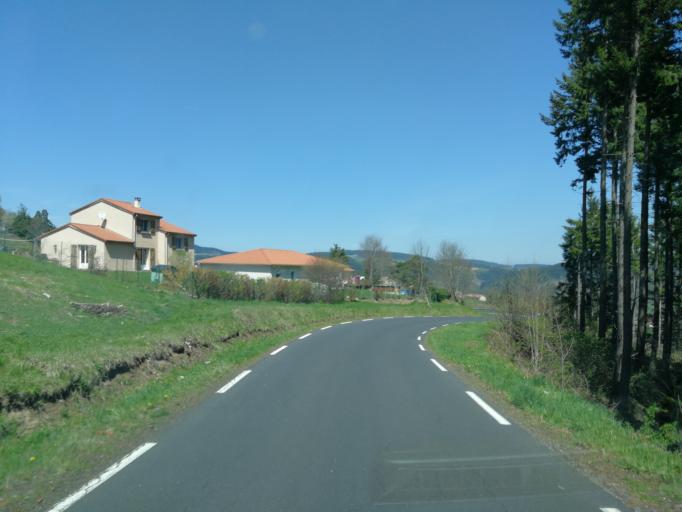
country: FR
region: Auvergne
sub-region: Departement de la Haute-Loire
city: Dunieres
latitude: 45.2048
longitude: 4.3443
